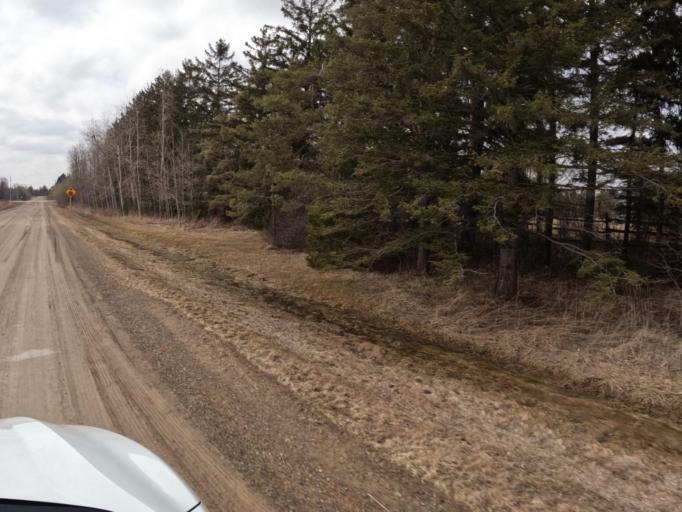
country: CA
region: Ontario
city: Shelburne
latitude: 44.0351
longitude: -80.2257
